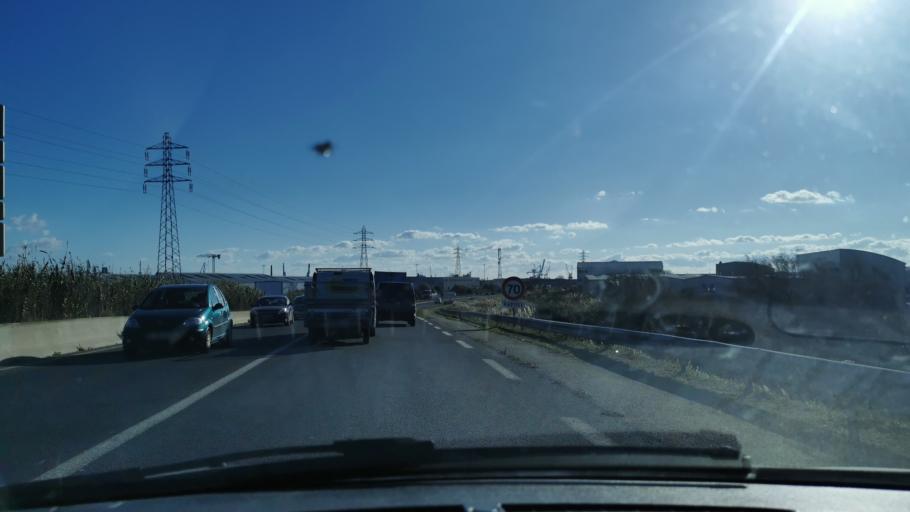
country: FR
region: Languedoc-Roussillon
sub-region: Departement de l'Herault
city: Sete
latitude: 43.4233
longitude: 3.7090
